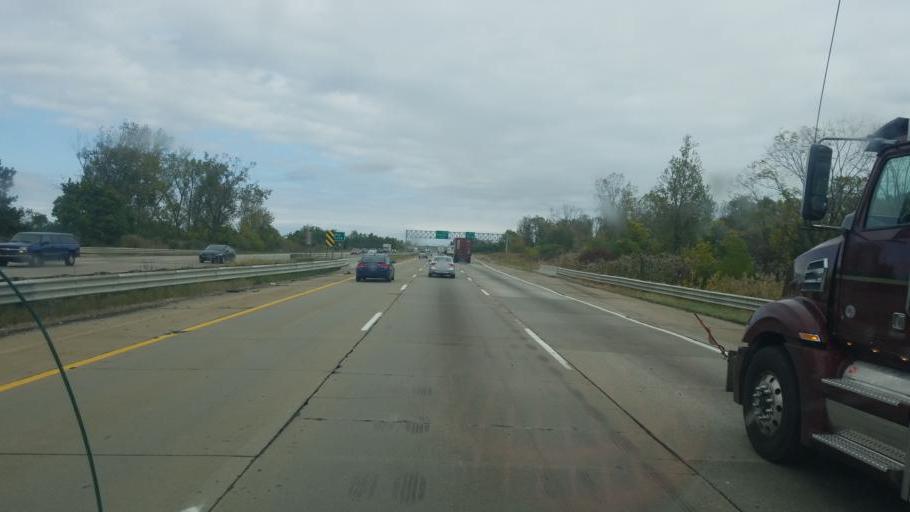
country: US
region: Michigan
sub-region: Monroe County
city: Luna Pier
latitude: 41.7883
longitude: -83.4671
